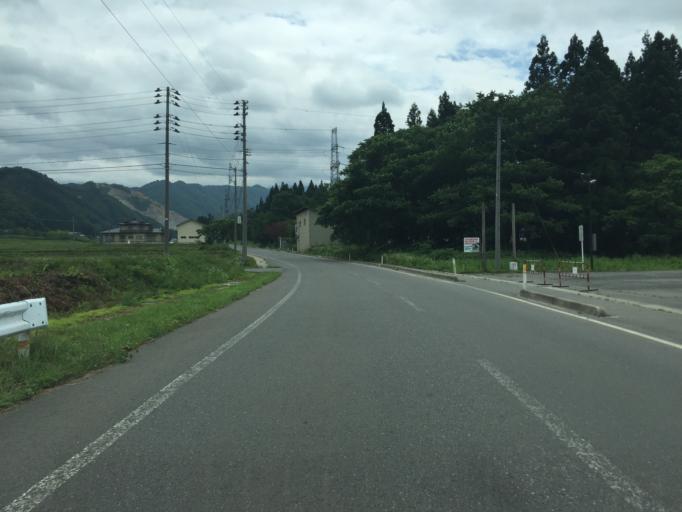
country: JP
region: Yamagata
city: Yonezawa
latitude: 37.8402
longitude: 140.0923
